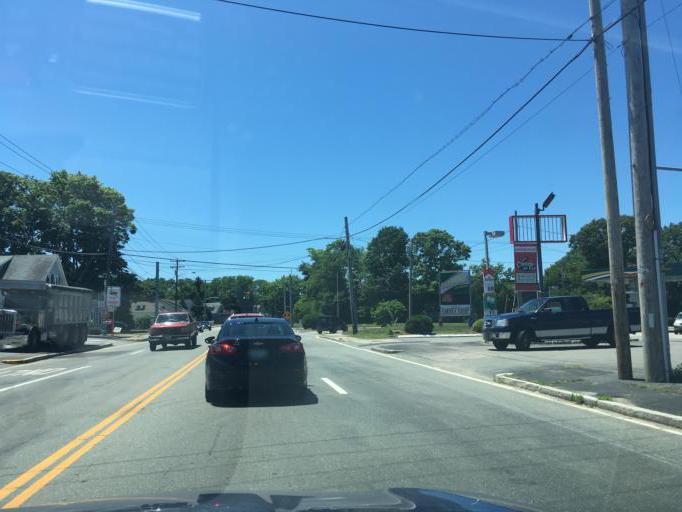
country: US
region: Rhode Island
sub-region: Kent County
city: Warwick
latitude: 41.7024
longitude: -71.3858
